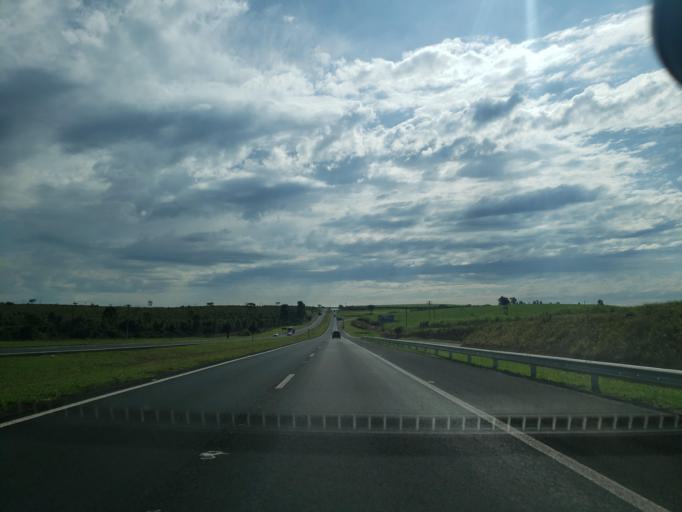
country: BR
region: Sao Paulo
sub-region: Cafelandia
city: Cafelandia
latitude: -21.8816
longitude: -49.5527
